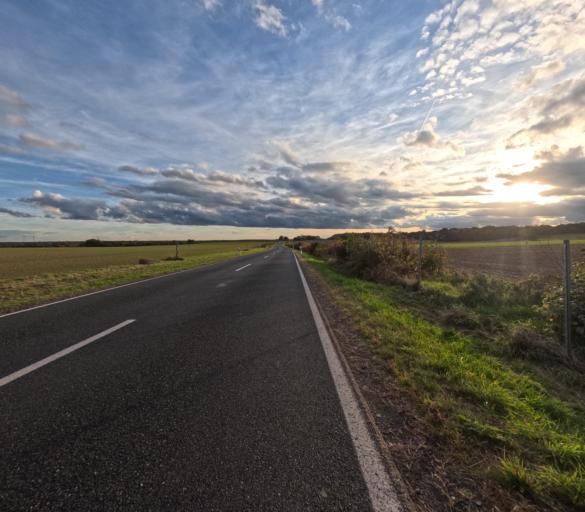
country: DE
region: Saxony
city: Grimma
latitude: 51.2546
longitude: 12.6801
